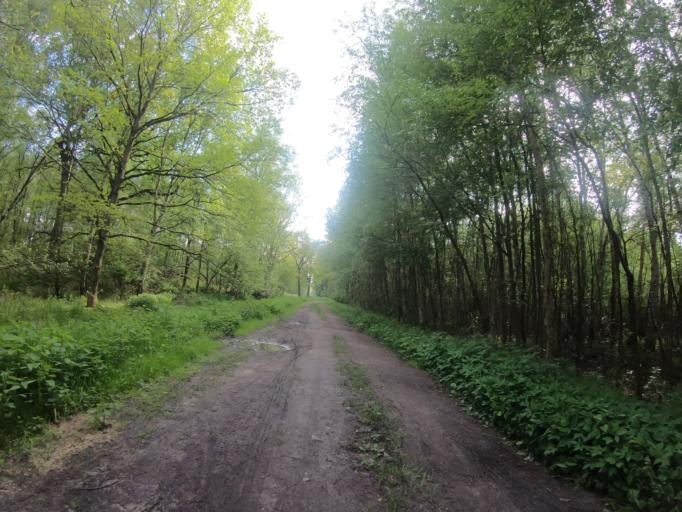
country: DE
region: Lower Saxony
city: Sassenburg
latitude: 52.5116
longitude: 10.6147
